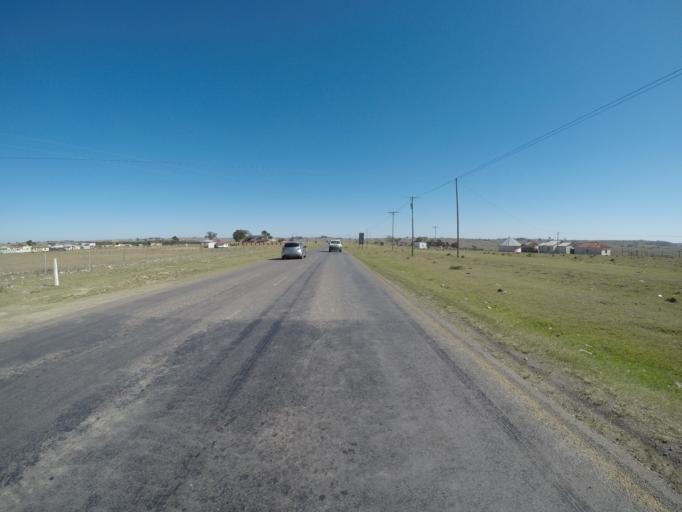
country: ZA
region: Eastern Cape
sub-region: OR Tambo District Municipality
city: Mthatha
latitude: -31.7857
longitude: 28.7418
